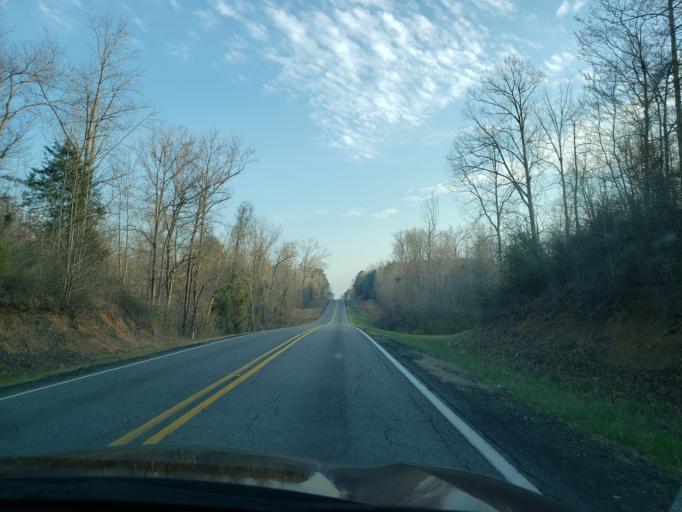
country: US
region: Alabama
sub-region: Hale County
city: Greensboro
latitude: 32.7941
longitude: -87.5912
